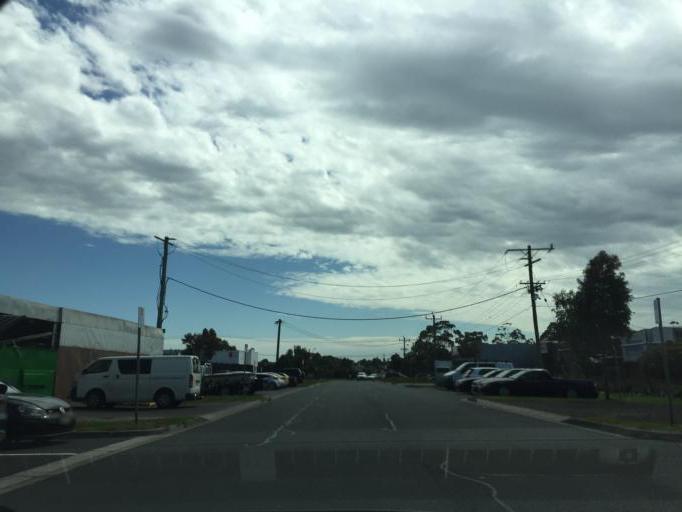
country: AU
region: Victoria
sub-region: Maribyrnong
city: Braybrook
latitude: -37.7797
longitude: 144.8574
